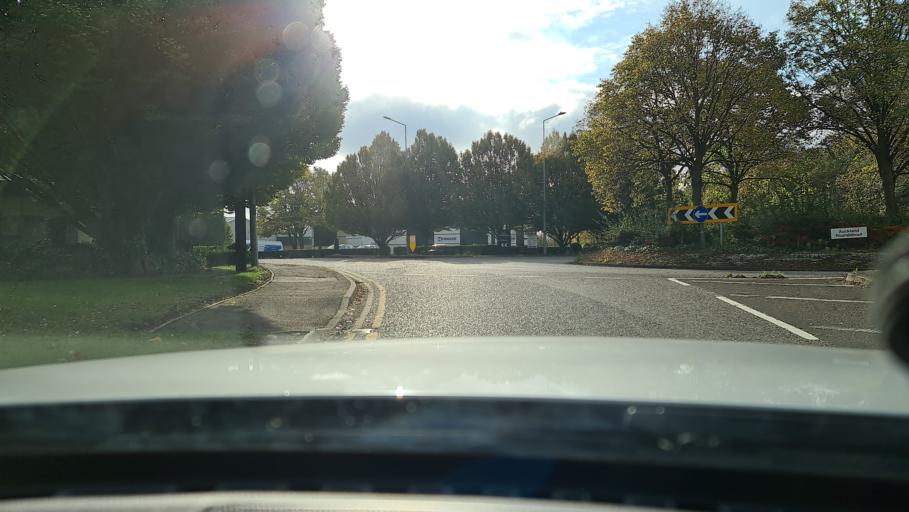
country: GB
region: England
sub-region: Buckinghamshire
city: Bletchley
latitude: 52.0109
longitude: -0.7217
